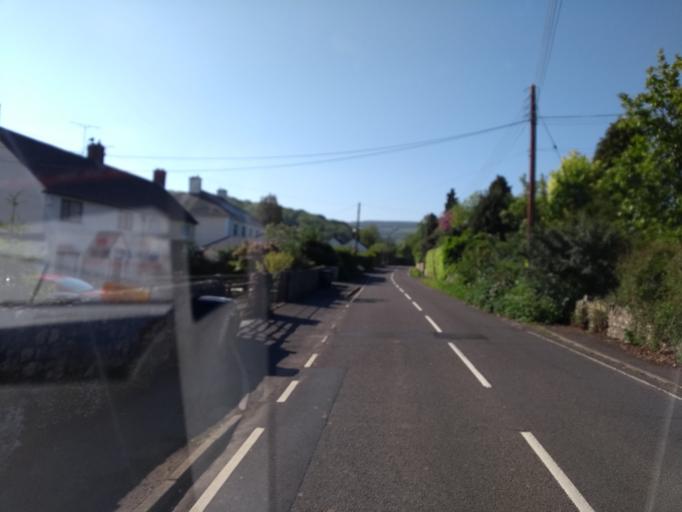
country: GB
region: England
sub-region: Somerset
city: Taunton
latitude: 50.9690
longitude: -3.0948
